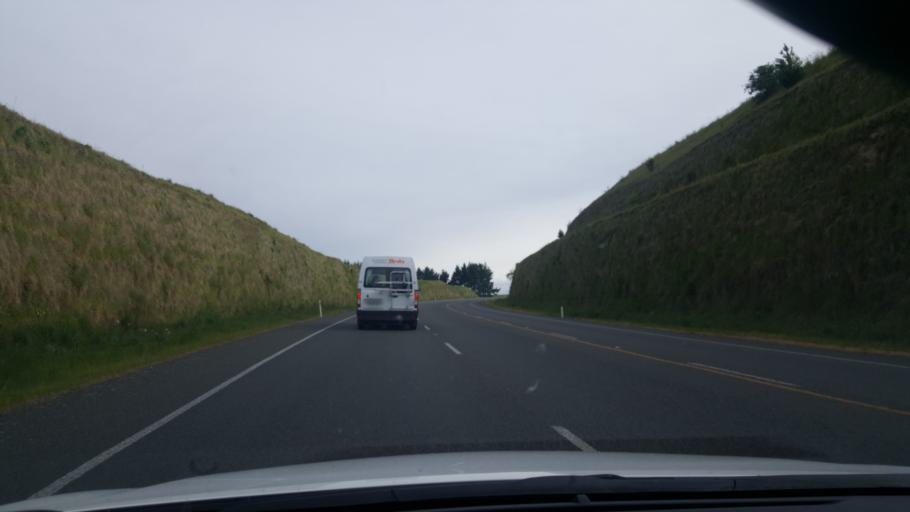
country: NZ
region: Waikato
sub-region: Taupo District
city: Taupo
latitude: -38.6399
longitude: 176.0984
